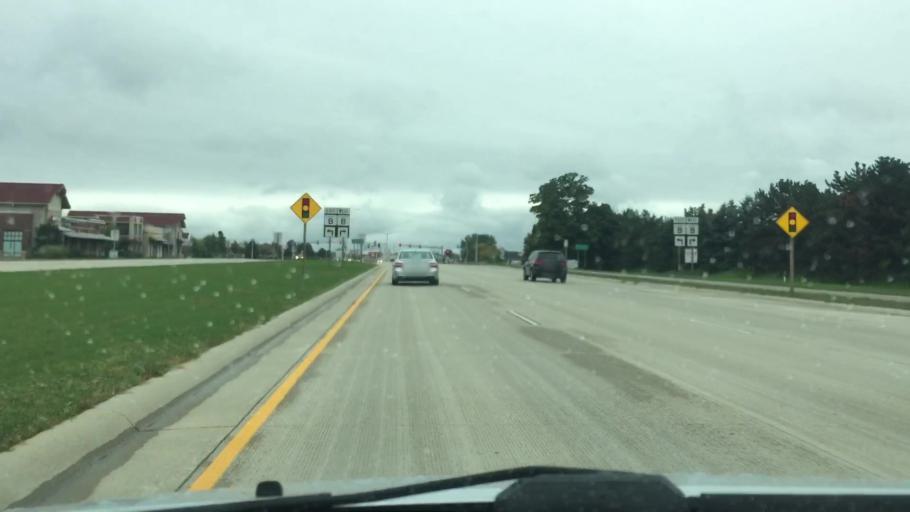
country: US
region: Wisconsin
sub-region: Waukesha County
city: Oconomowoc
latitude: 43.0794
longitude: -88.4708
